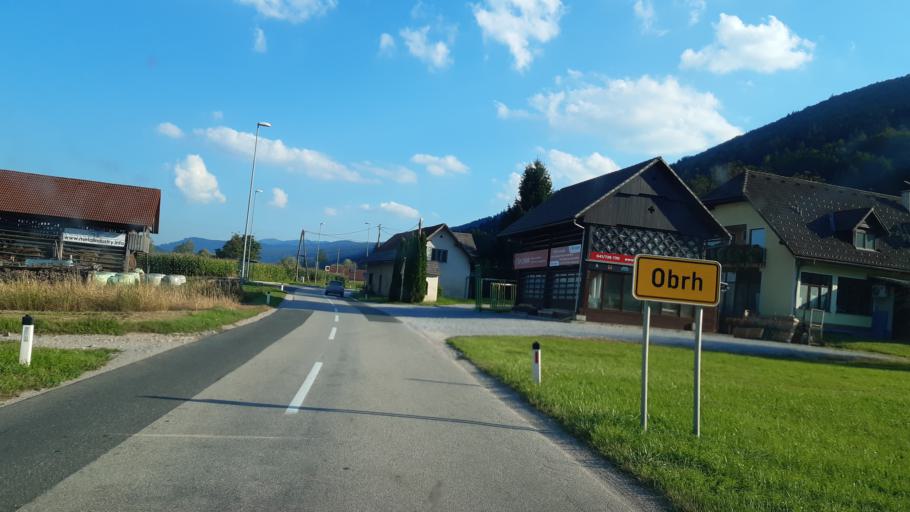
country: SI
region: Dolenjske Toplice
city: Dolenjske Toplice
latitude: 45.7521
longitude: 15.0349
